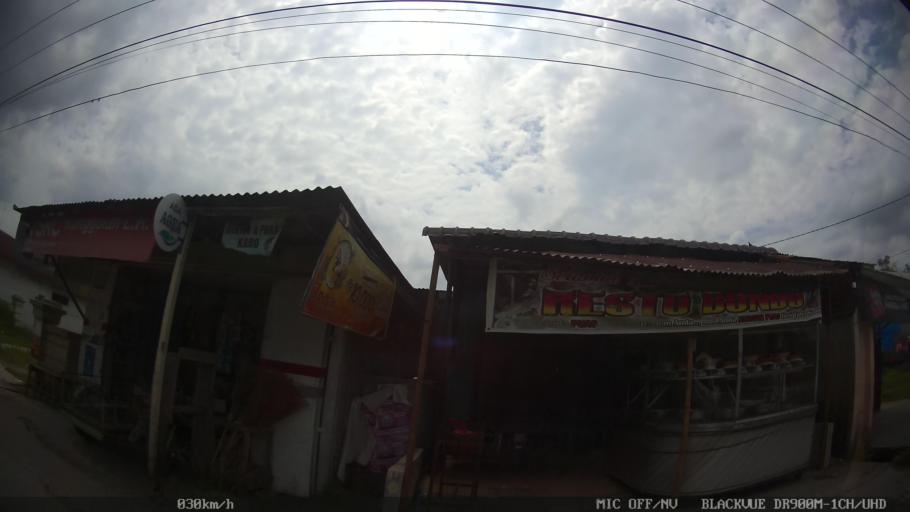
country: ID
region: North Sumatra
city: Sunggal
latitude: 3.6246
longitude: 98.5937
